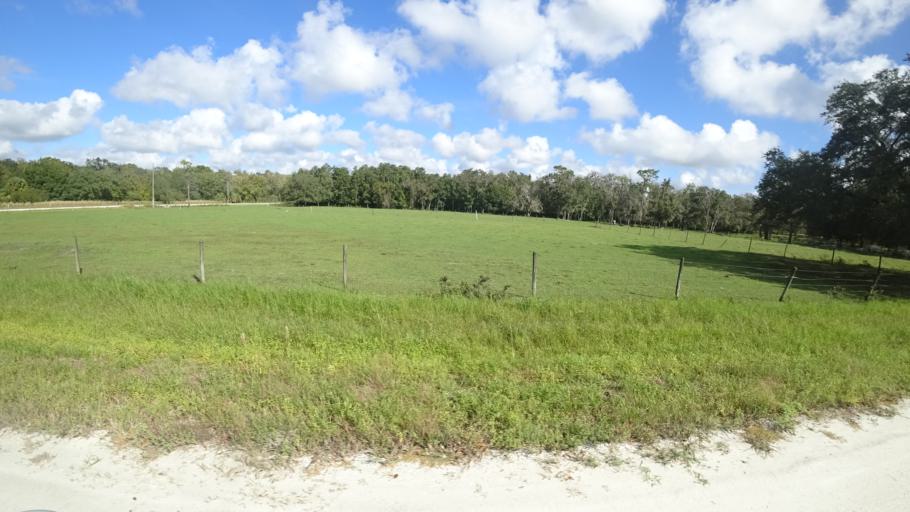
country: US
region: Florida
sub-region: Sarasota County
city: Lake Sarasota
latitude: 27.3358
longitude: -82.2046
